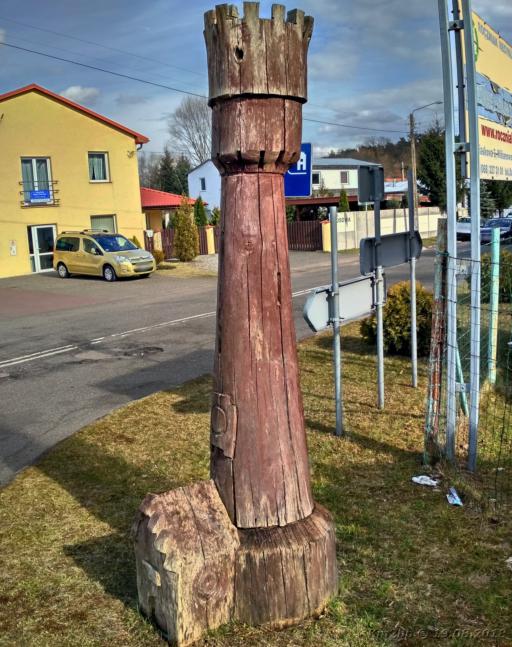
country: PL
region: Lubusz
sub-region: Powiat zielonogorski
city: Ochla
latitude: 51.9185
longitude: 15.4372
